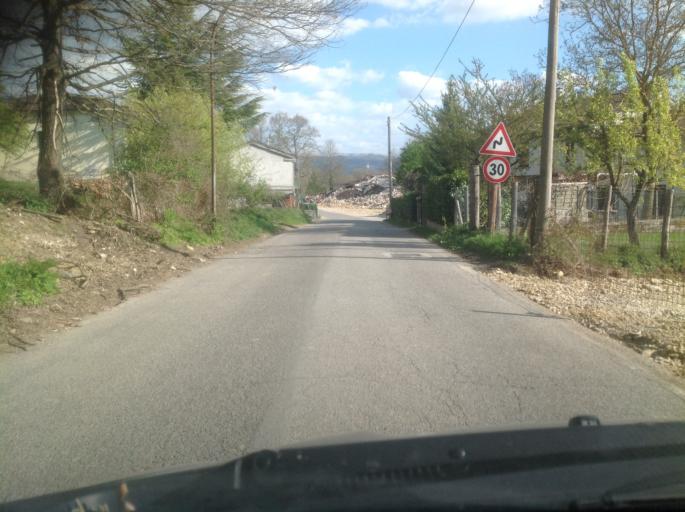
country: IT
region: Latium
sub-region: Provincia di Rieti
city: Amatrice
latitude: 42.6650
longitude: 13.2891
